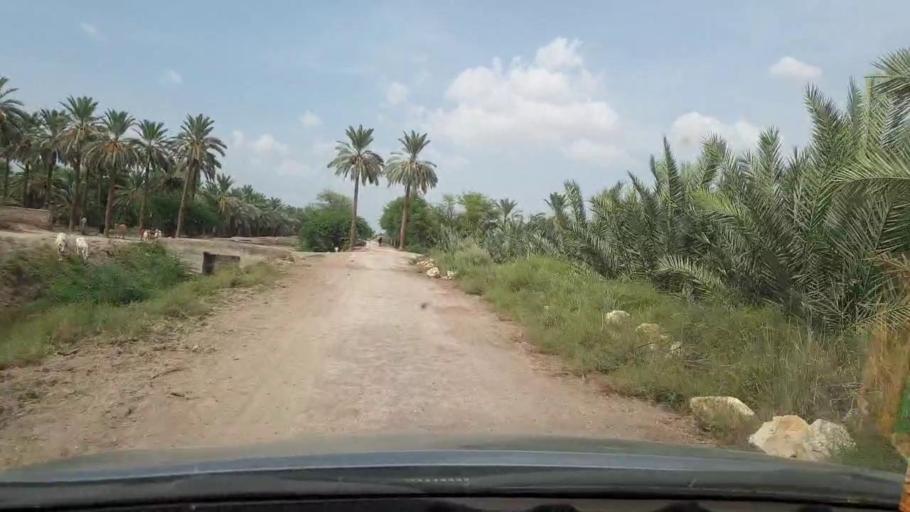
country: PK
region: Sindh
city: Khairpur
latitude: 27.5209
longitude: 68.8836
